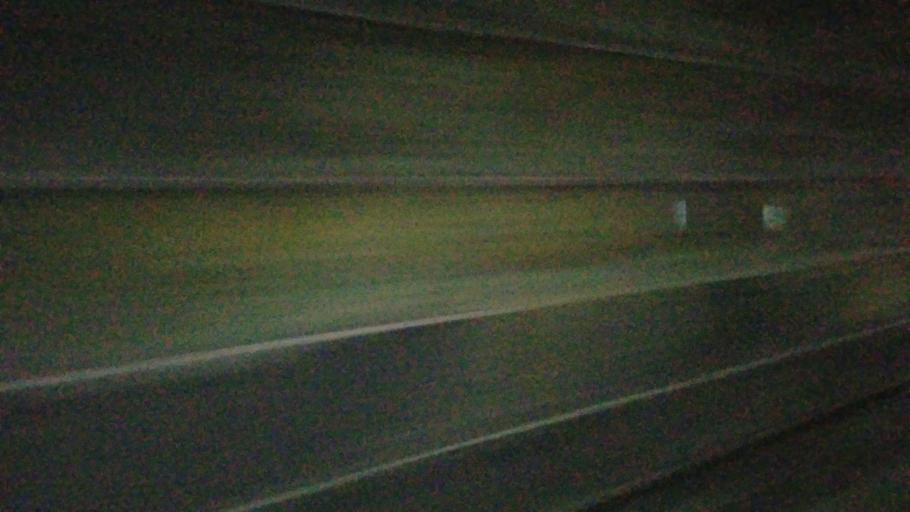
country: US
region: Pennsylvania
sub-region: Allegheny County
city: Pittsburgh
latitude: 40.4506
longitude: -80.0101
